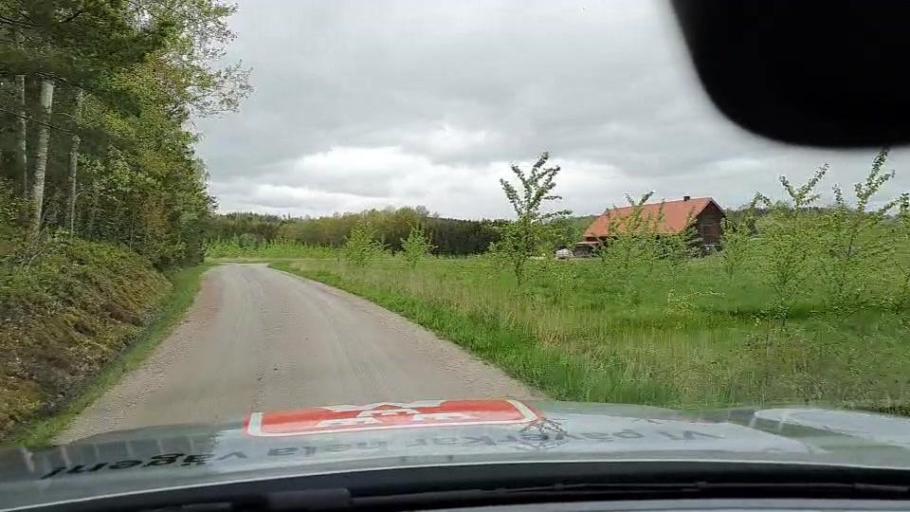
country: SE
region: Soedermanland
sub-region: Nykopings Kommun
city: Svalsta
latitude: 58.6329
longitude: 16.9379
